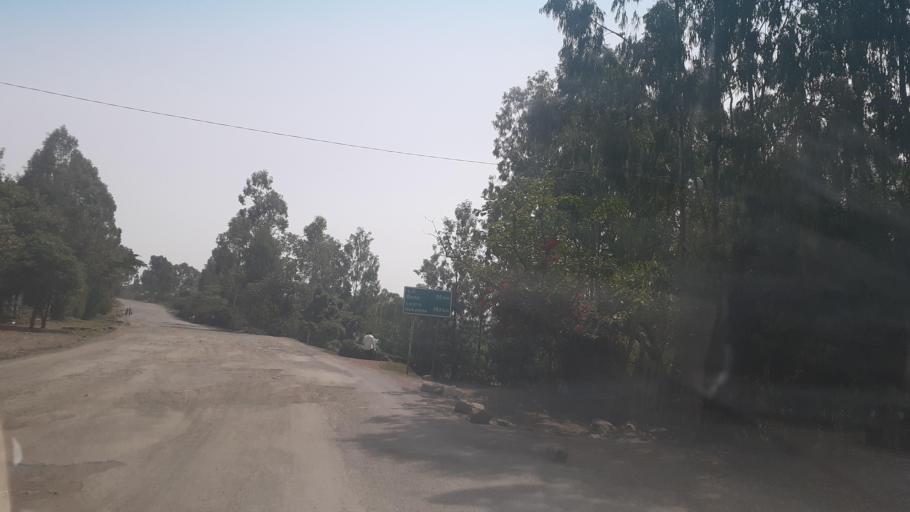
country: ET
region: Oromiya
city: Guder
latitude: 8.9682
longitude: 37.7553
